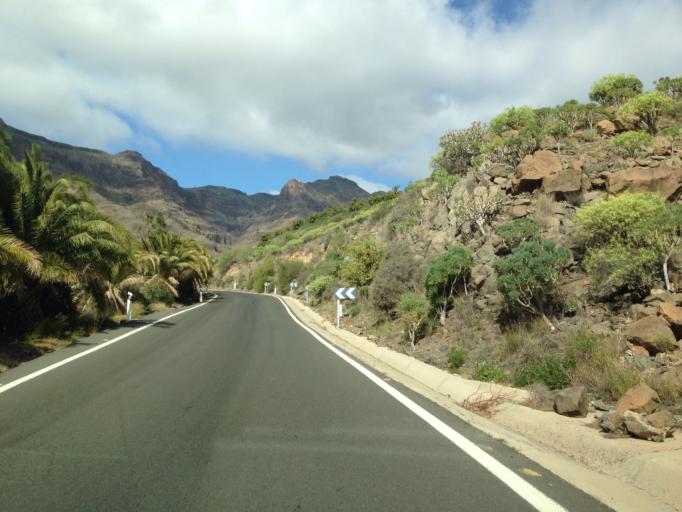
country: ES
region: Canary Islands
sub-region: Provincia de Las Palmas
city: Santa Lucia
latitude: 27.8605
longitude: -15.5654
